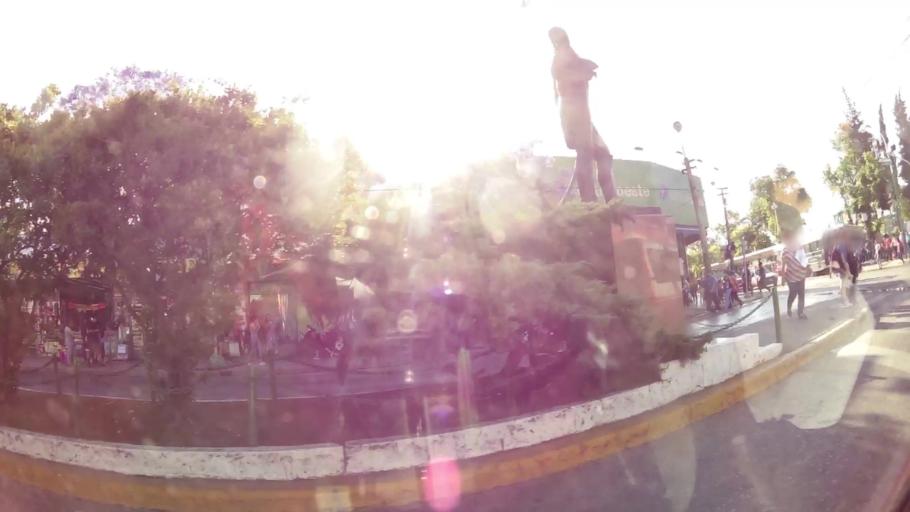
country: AR
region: Buenos Aires
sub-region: Partido de Merlo
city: Merlo
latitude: -34.6655
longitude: -58.7275
